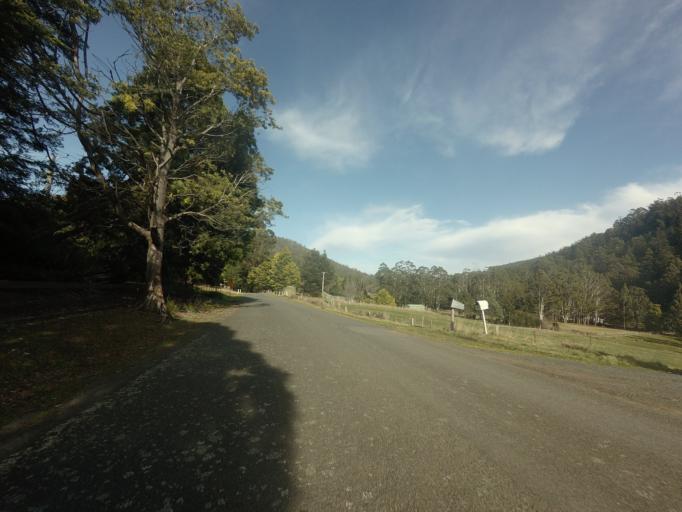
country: AU
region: Tasmania
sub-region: Huon Valley
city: Huonville
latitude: -43.0479
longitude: 147.1110
